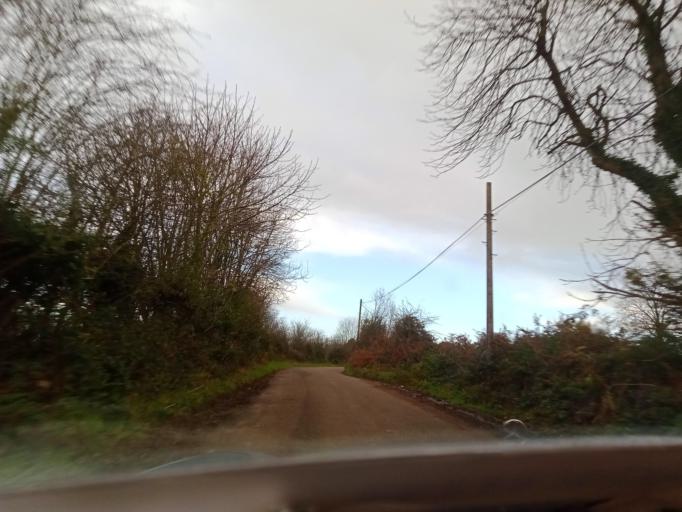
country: IE
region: Munster
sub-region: Waterford
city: Waterford
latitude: 52.3136
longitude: -7.0474
